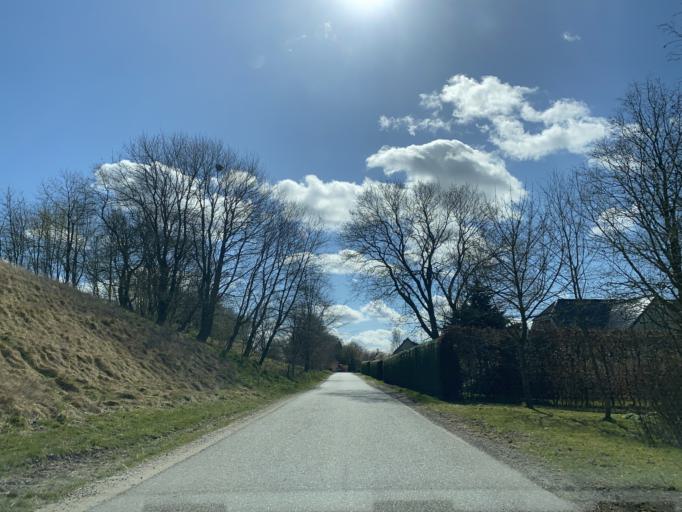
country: DK
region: Central Jutland
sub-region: Favrskov Kommune
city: Ulstrup
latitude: 56.3426
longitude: 9.7887
